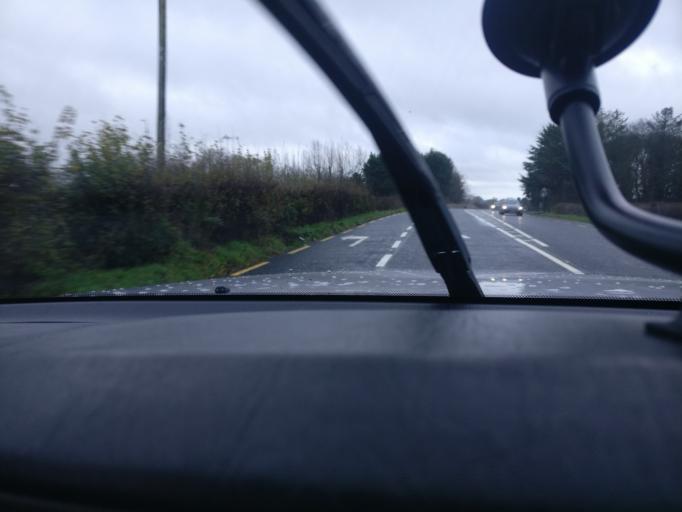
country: IE
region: Leinster
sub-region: An Mhi
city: Enfield
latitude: 53.4225
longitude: -6.8622
